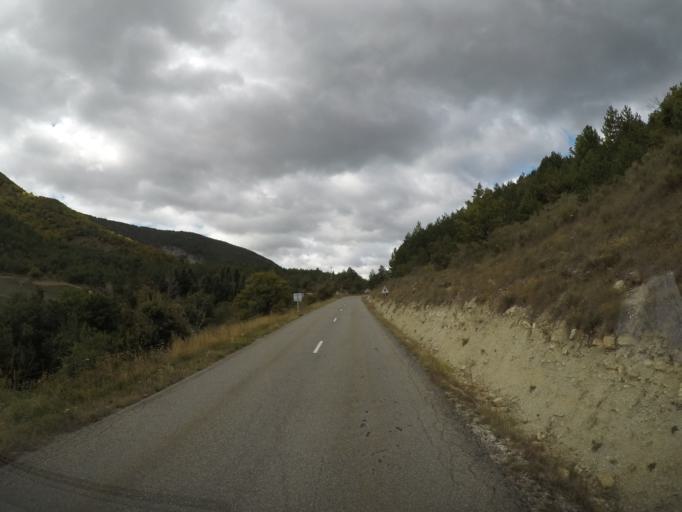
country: FR
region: Provence-Alpes-Cote d'Azur
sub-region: Departement du Vaucluse
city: Sault
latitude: 44.1791
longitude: 5.5711
